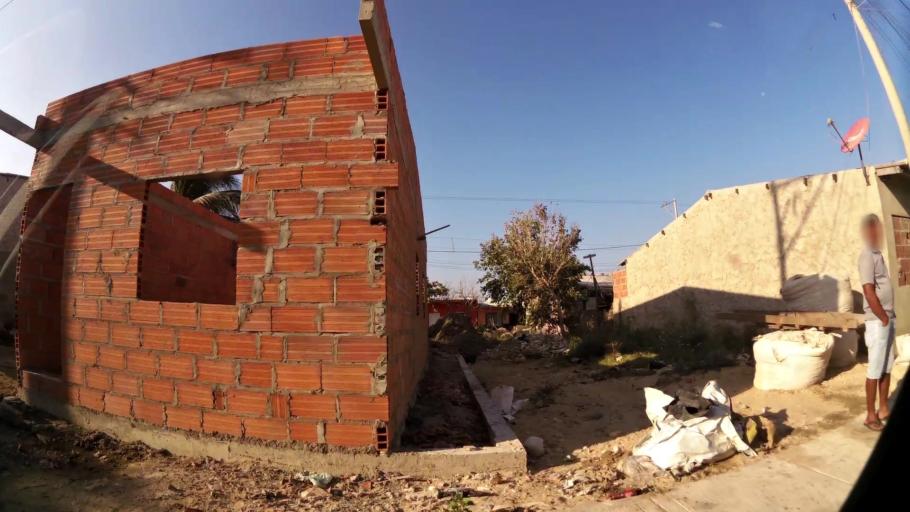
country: CO
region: Atlantico
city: Barranquilla
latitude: 11.0435
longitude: -74.8297
